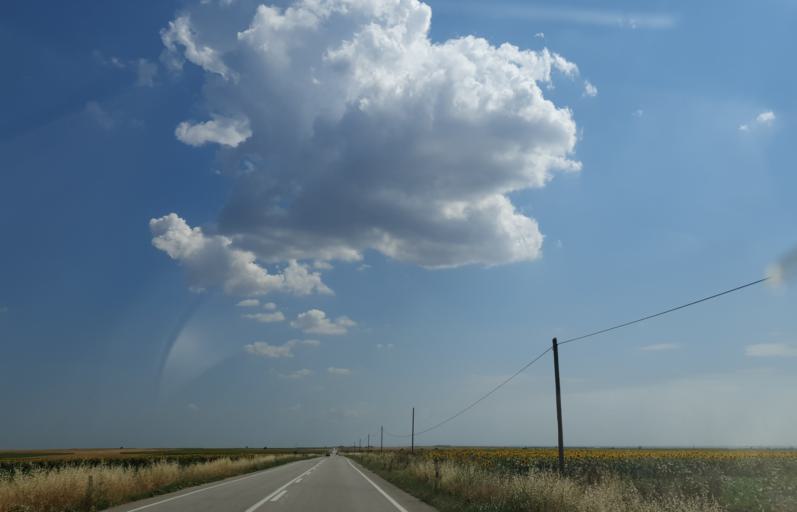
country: TR
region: Kirklareli
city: Buyukkaristiran
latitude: 41.4273
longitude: 27.5815
